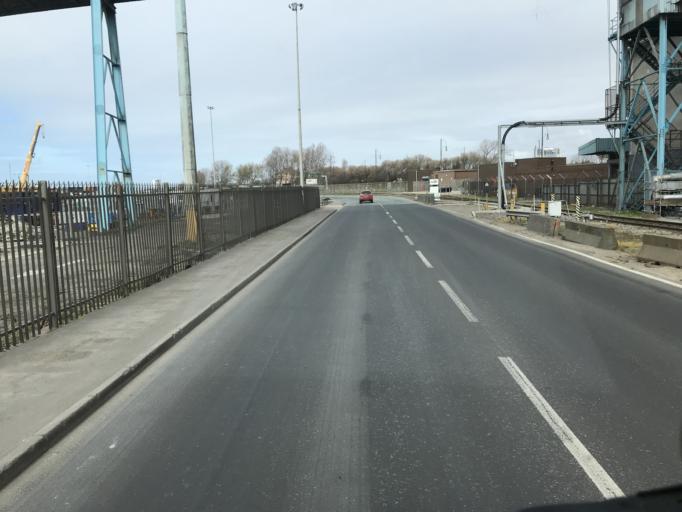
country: GB
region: England
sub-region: Sefton
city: Bootle
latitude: 53.4598
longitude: -3.0131
